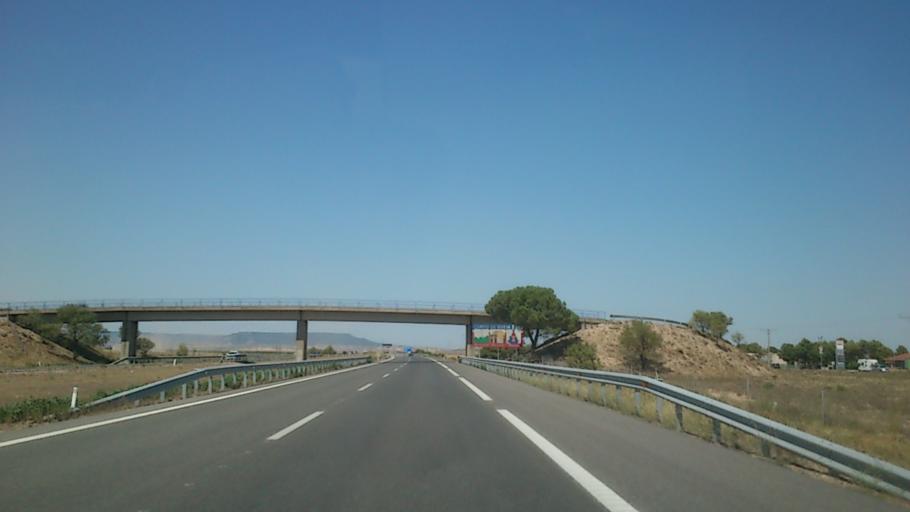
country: ES
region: Aragon
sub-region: Provincia de Zaragoza
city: Gallur
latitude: 41.8436
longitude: -1.3516
